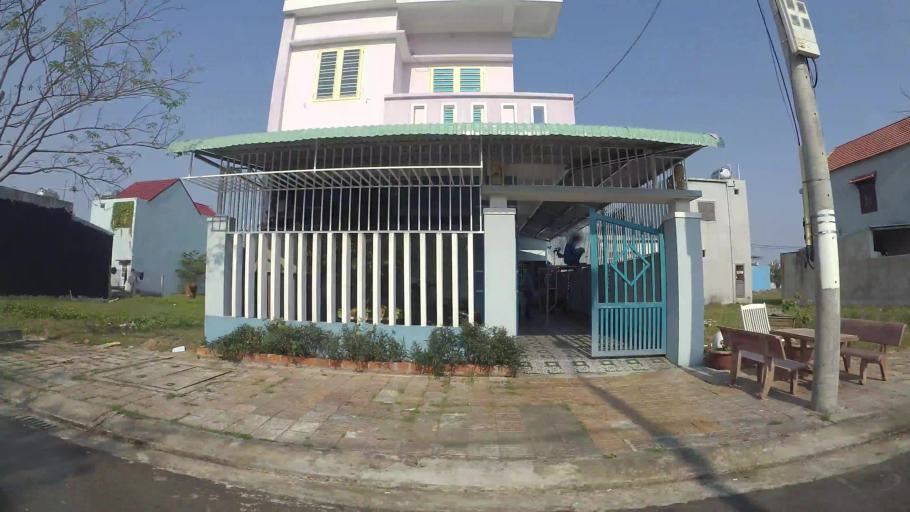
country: VN
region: Quang Nam
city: Quang Nam
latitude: 15.9467
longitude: 108.2580
